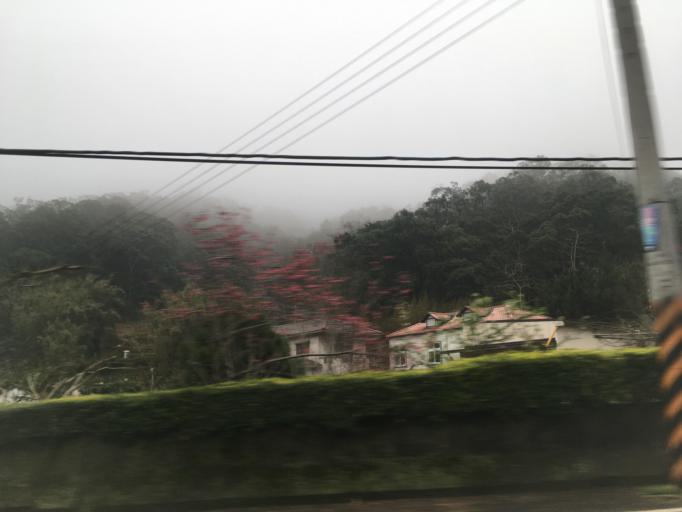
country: TW
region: Taiwan
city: Fengyuan
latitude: 24.4127
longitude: 120.7530
